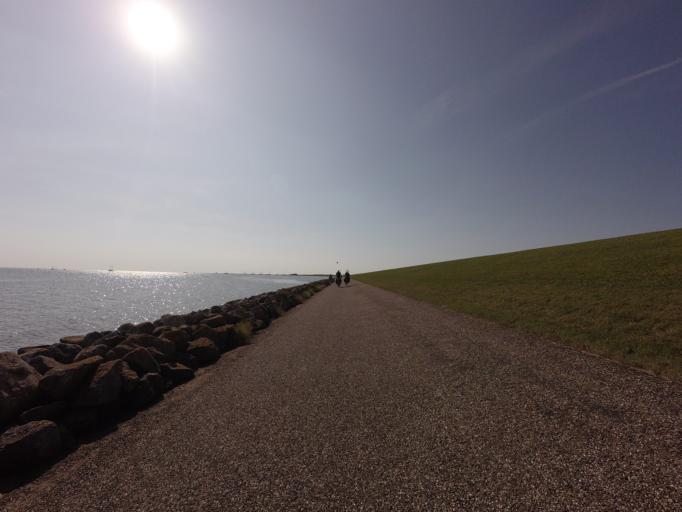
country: NL
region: Friesland
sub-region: Gemeente Schiermonnikoog
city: Schiermonnikoog
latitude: 53.4724
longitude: 6.1850
